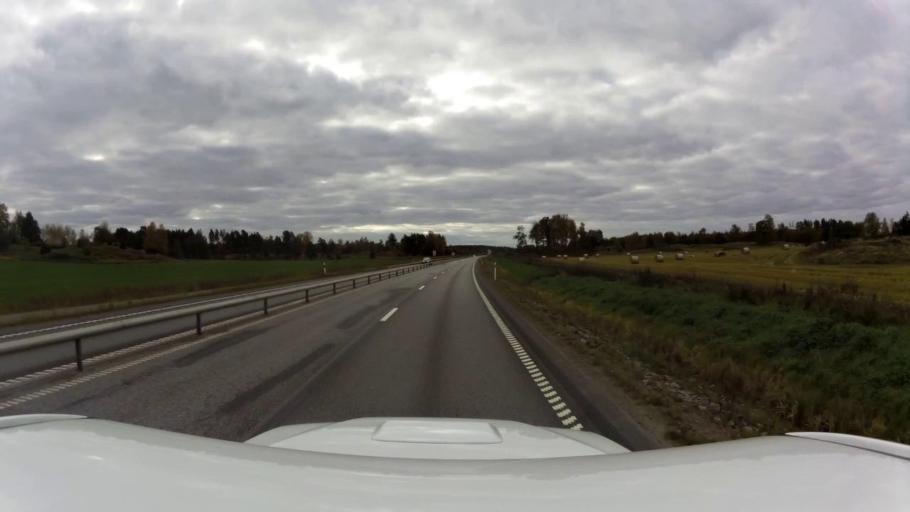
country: SE
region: OEstergoetland
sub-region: Linkopings Kommun
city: Malmslatt
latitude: 58.3209
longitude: 15.5677
